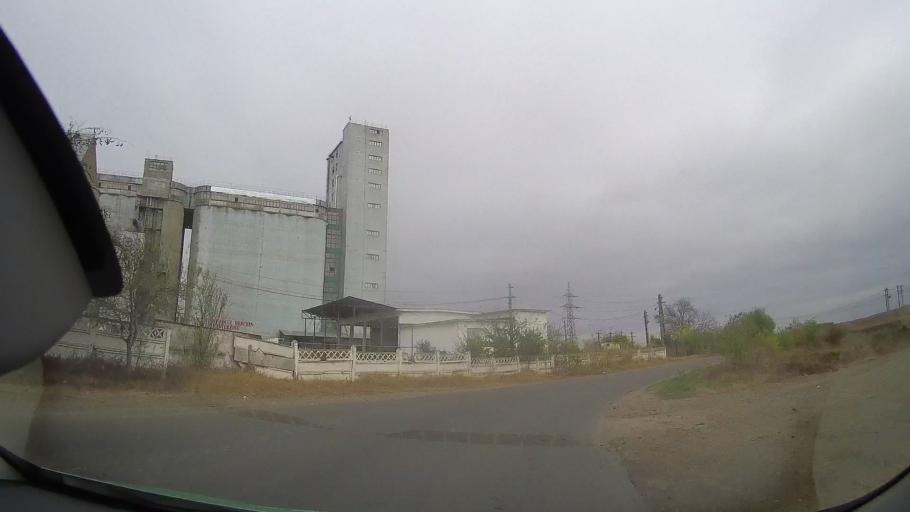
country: RO
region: Braila
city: Dudesti
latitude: 44.8937
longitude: 27.4340
